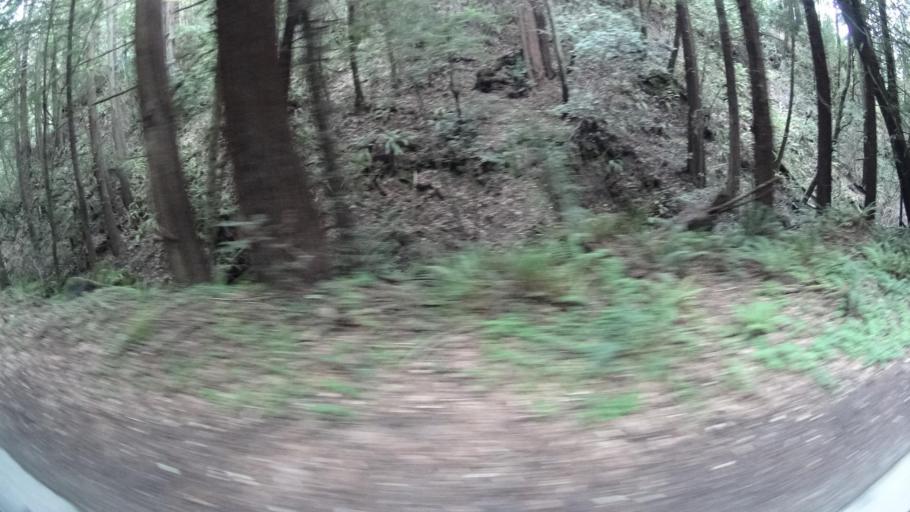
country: US
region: California
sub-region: Humboldt County
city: Redway
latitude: 40.3366
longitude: -123.9032
